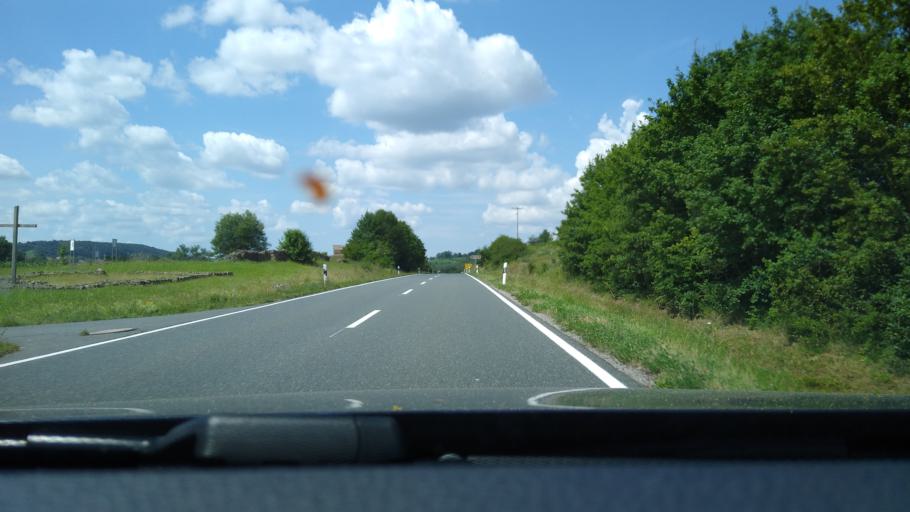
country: DE
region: Bavaria
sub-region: Regierungsbezirk Mittelfranken
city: Neuhof an der Zenn
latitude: 49.4651
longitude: 10.6584
